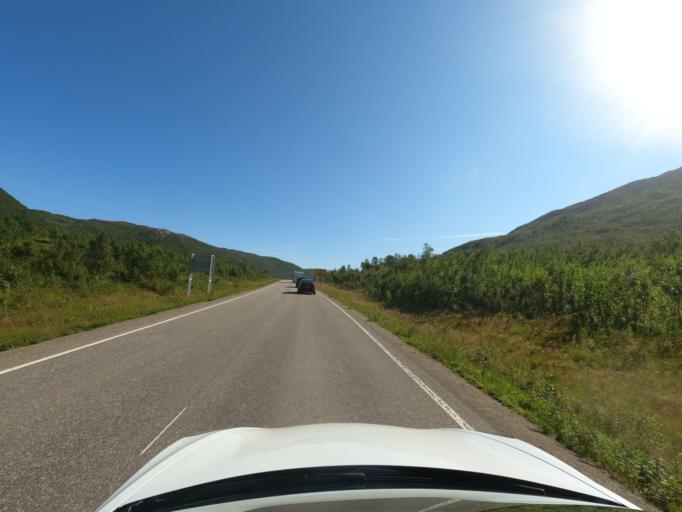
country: NO
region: Nordland
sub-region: Lodingen
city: Lodingen
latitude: 68.5287
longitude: 15.7590
